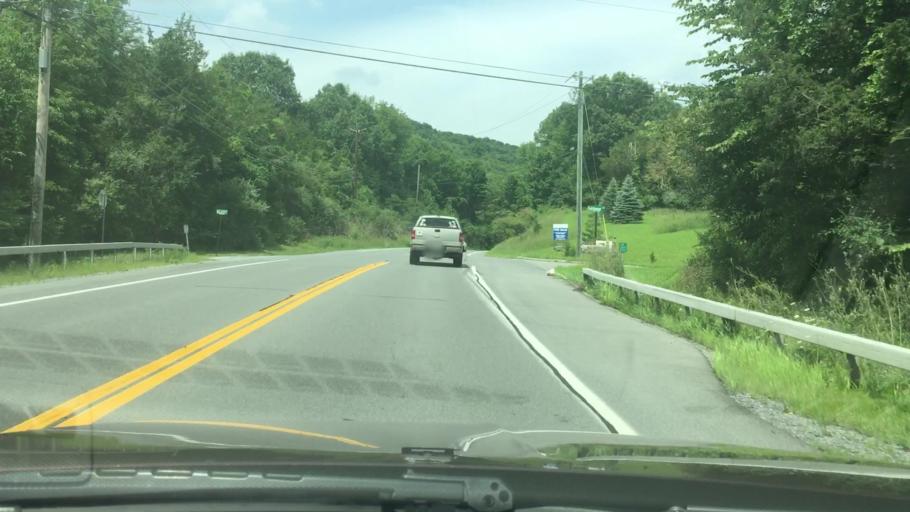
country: US
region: New York
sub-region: Dutchess County
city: Hillside Lake
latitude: 41.6309
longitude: -73.7046
